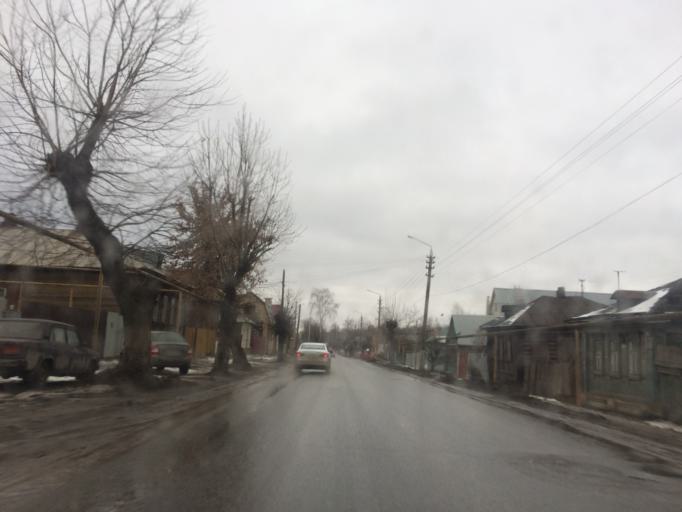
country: RU
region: Tula
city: Tula
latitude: 54.1966
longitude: 37.6380
